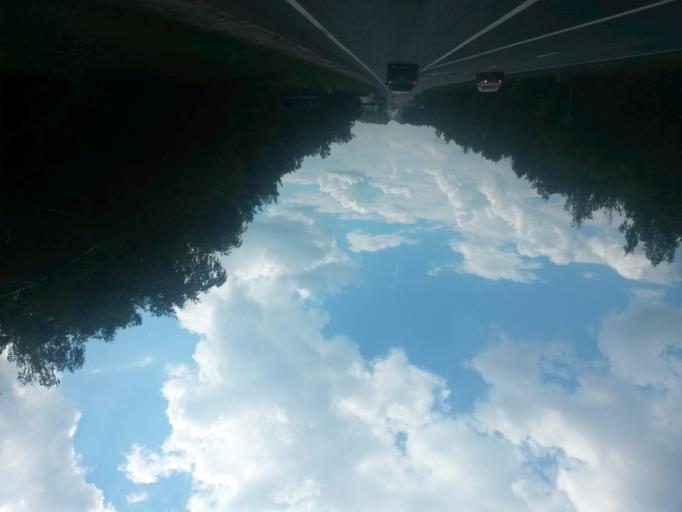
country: RU
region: Moskovskaya
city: Belyye Stolby
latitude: 55.3435
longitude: 37.7994
